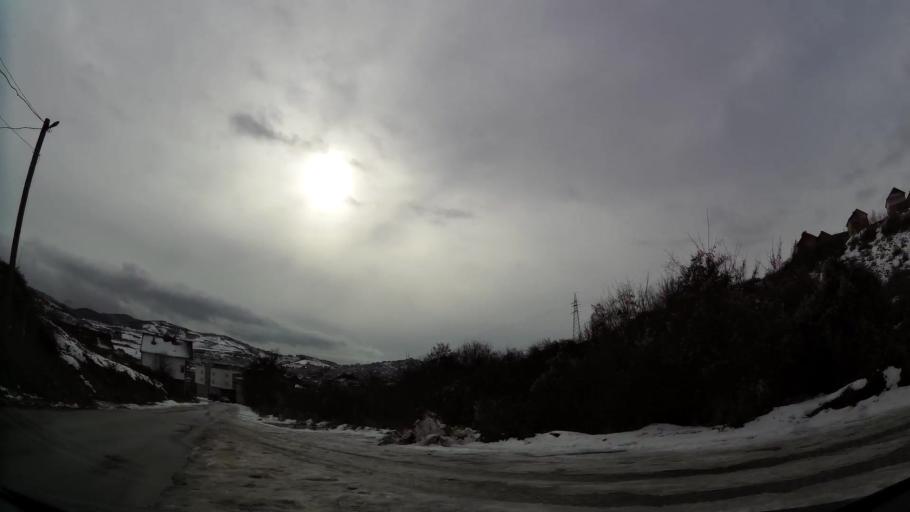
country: XK
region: Pristina
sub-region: Komuna e Prishtines
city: Pristina
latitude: 42.6904
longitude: 21.1773
